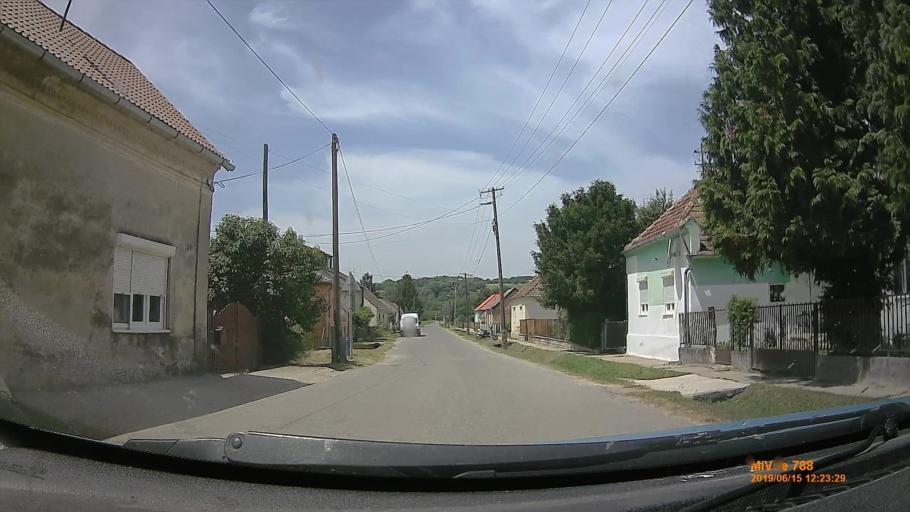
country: HU
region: Baranya
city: Buekkoesd
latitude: 46.1104
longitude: 18.0024
